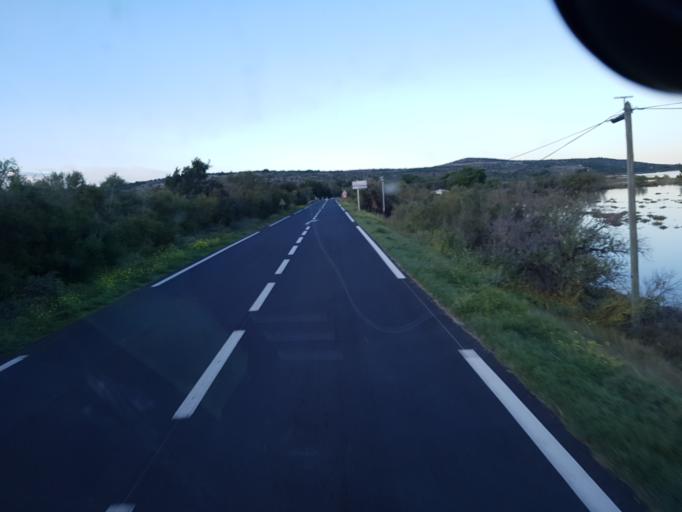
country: FR
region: Languedoc-Roussillon
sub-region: Departement de l'Aude
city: Sigean
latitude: 42.9698
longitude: 2.9993
